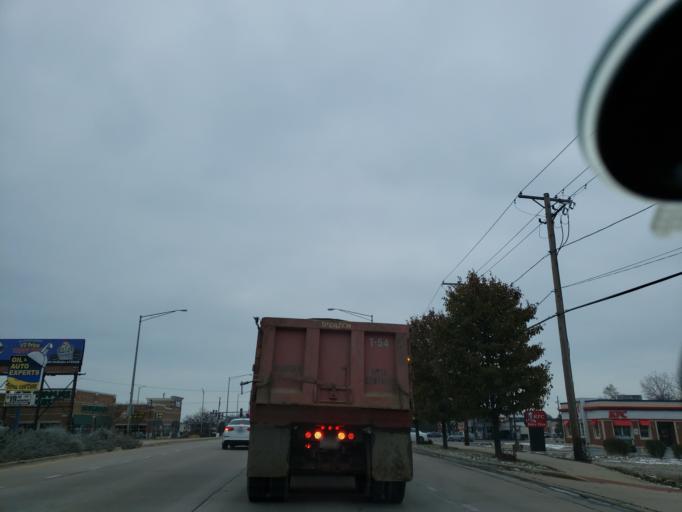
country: US
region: Illinois
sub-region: Cook County
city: Orland Hills
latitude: 41.6013
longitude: -87.8499
